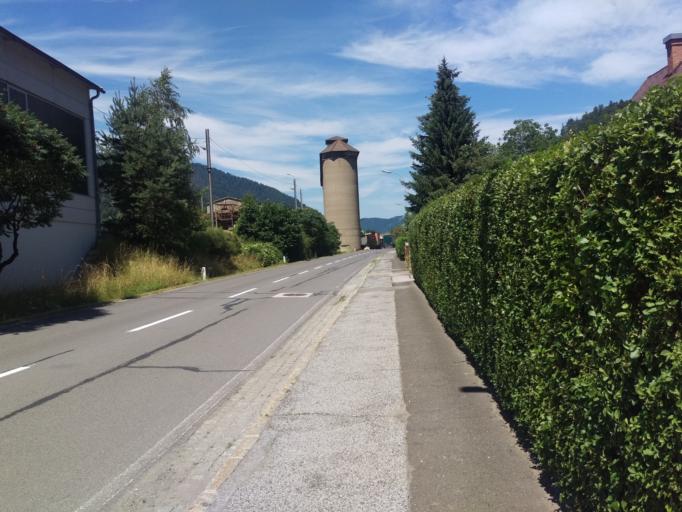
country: AT
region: Styria
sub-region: Politischer Bezirk Graz-Umgebung
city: Rothelstein
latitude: 47.3322
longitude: 15.3605
